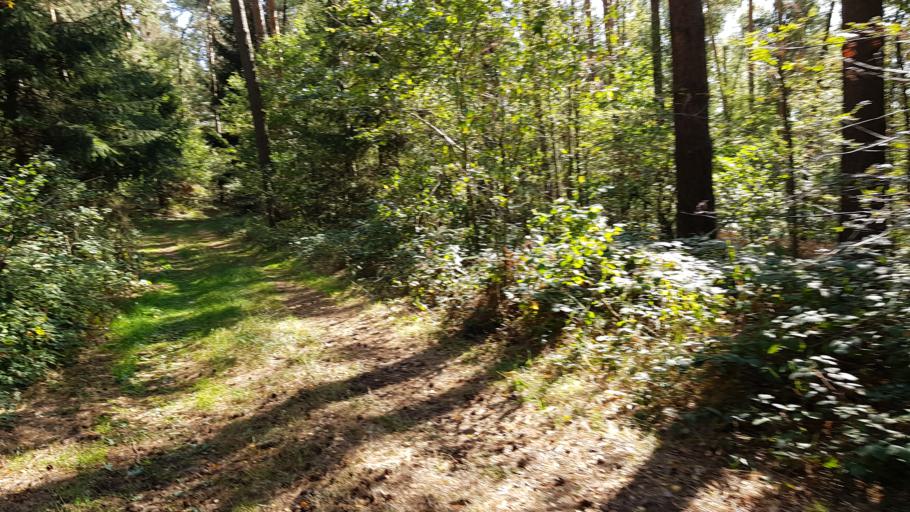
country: DE
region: Saxony
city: Grossnaundorf
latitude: 51.2153
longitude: 13.9591
